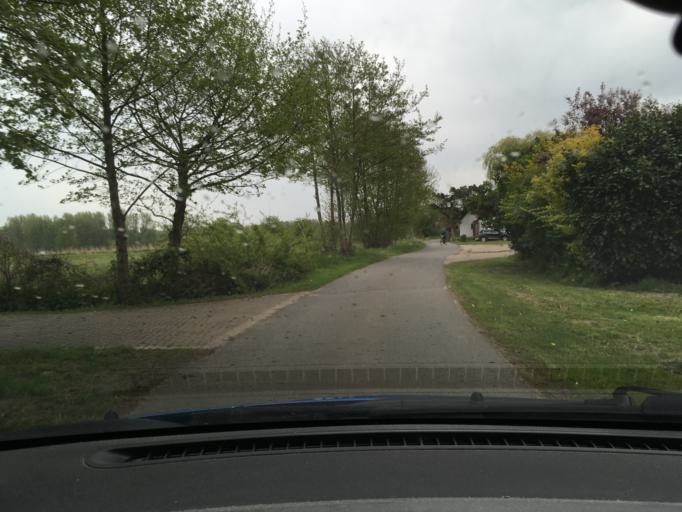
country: DE
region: Lower Saxony
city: Wittorf
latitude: 53.3337
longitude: 10.3822
